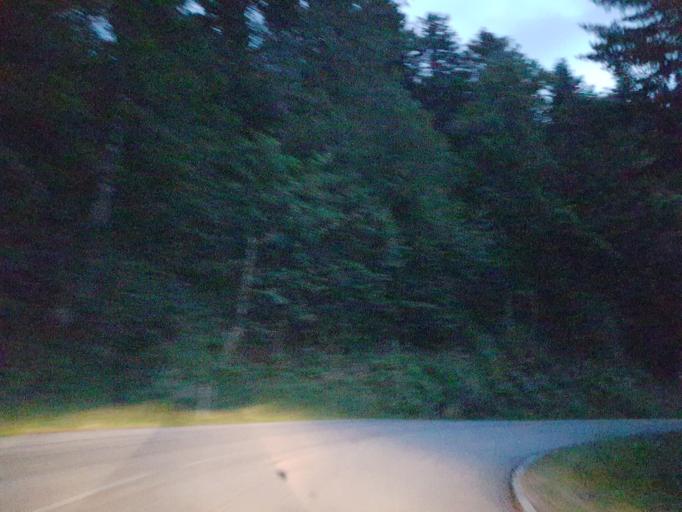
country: FR
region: Lorraine
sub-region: Departement des Vosges
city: Xonrupt-Longemer
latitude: 48.0619
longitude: 6.9963
